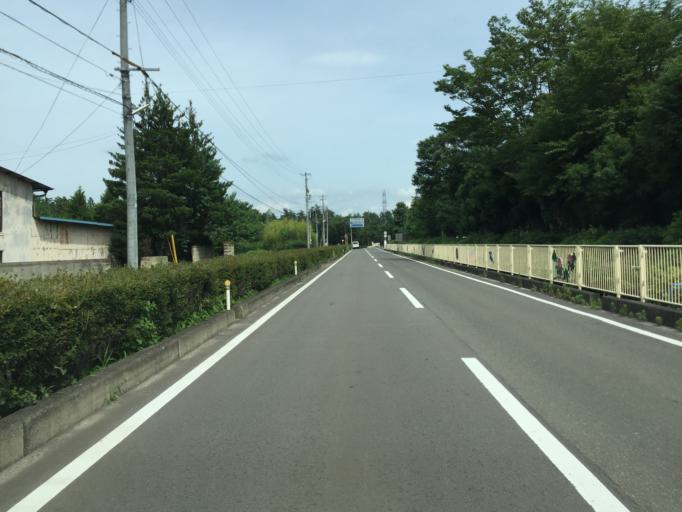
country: JP
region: Fukushima
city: Fukushima-shi
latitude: 37.7256
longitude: 140.3645
